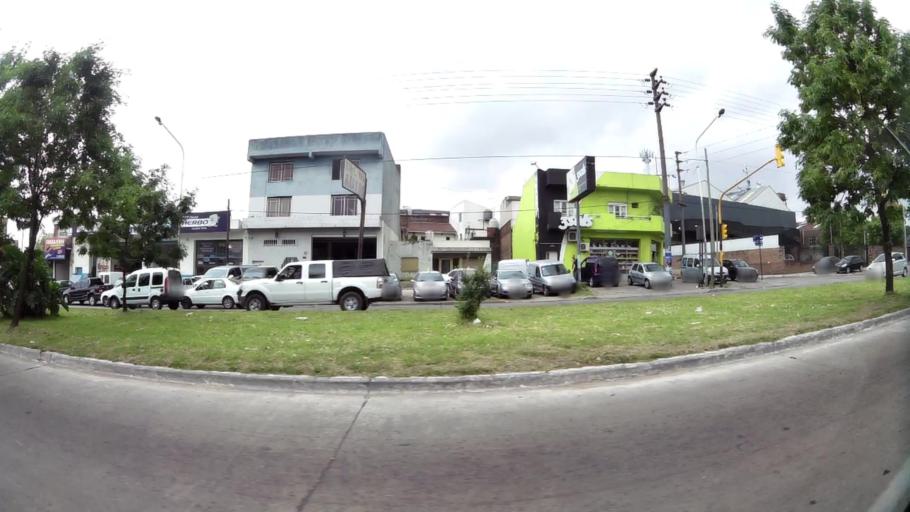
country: AR
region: Buenos Aires
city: San Justo
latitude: -34.6980
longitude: -58.5381
